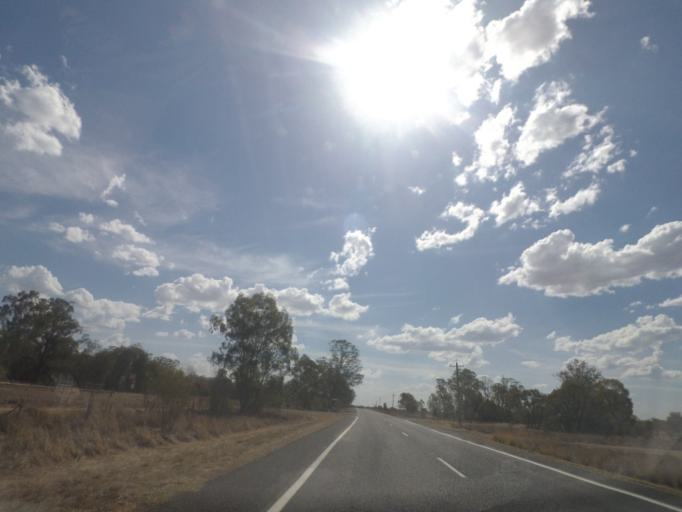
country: AU
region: New South Wales
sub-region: Moree Plains
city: Boggabilla
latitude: -28.4144
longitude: 151.1471
